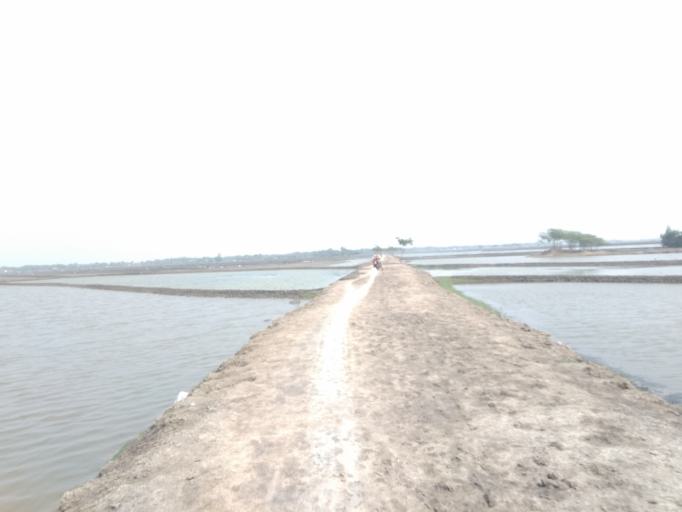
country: IN
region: West Bengal
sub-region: North 24 Parganas
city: Taki
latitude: 22.2715
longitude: 89.2804
